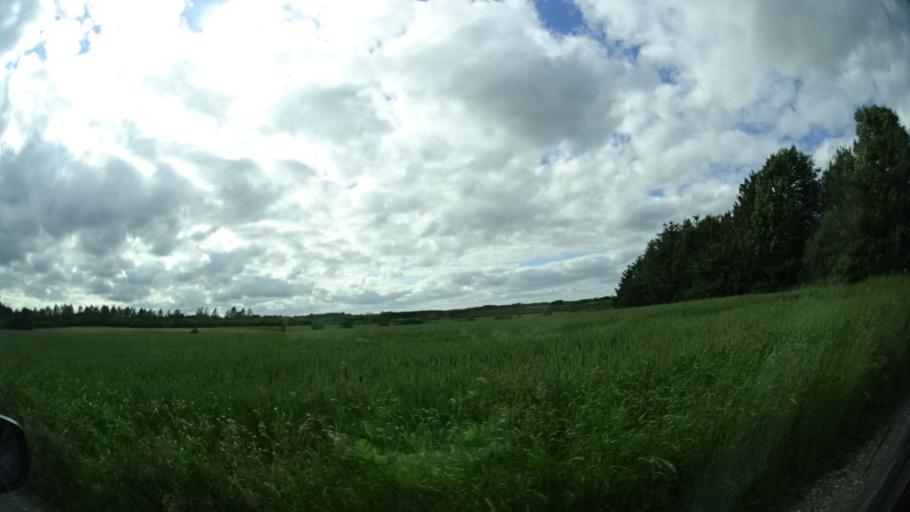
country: DK
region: Central Jutland
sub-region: Syddjurs Kommune
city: Ryomgard
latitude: 56.4311
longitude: 10.6186
